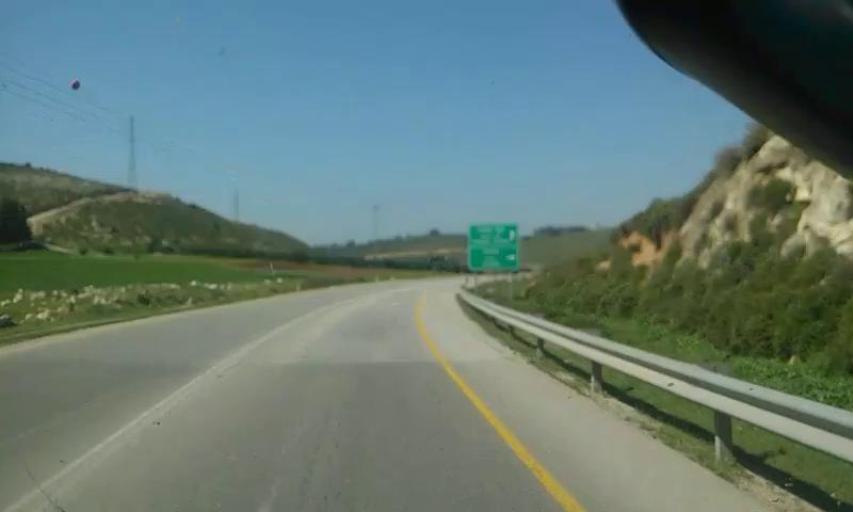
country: PS
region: West Bank
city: Idhna
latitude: 31.5831
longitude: 34.9733
